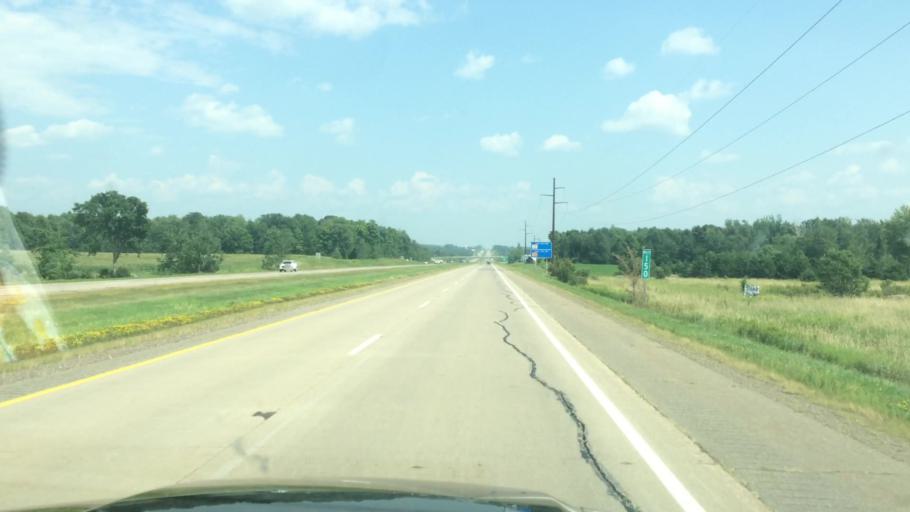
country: US
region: Wisconsin
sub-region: Marathon County
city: Edgar
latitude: 44.9443
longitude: -89.9794
